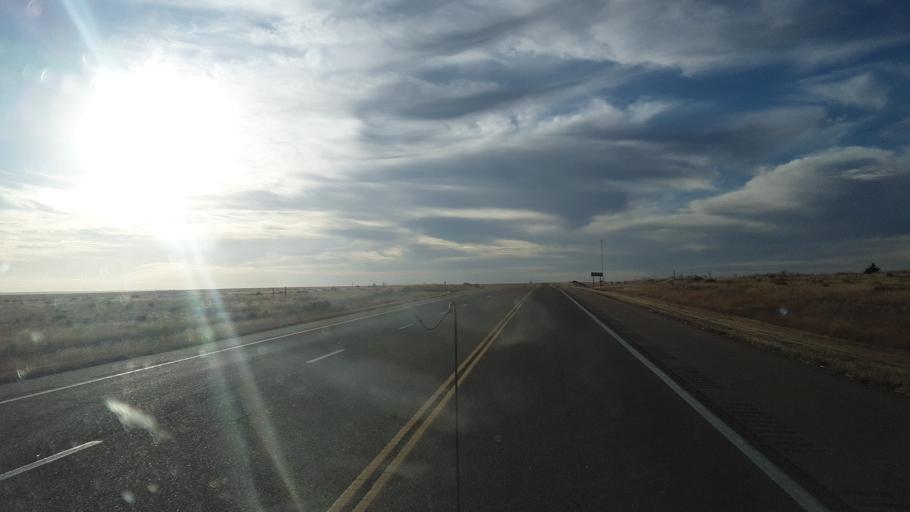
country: US
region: Kansas
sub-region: Kearny County
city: Lakin
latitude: 37.9443
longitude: -101.4948
